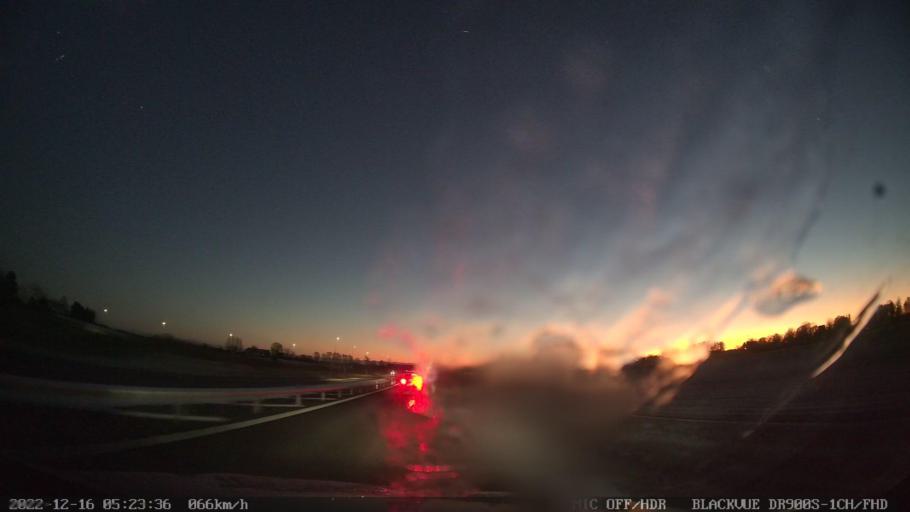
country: SE
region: Skane
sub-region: Ystads Kommun
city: Kopingebro
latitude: 55.4783
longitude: 13.8834
